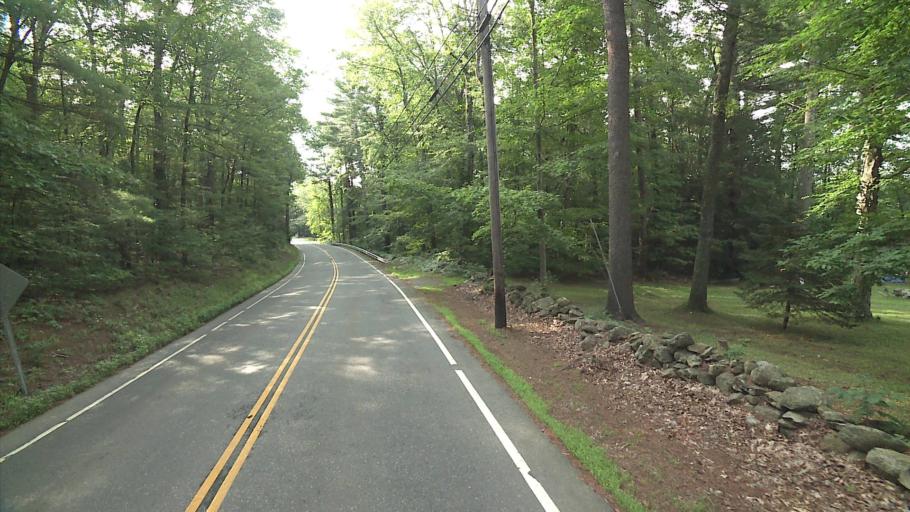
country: US
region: Massachusetts
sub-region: Worcester County
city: Southbridge
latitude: 41.9751
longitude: -72.0708
